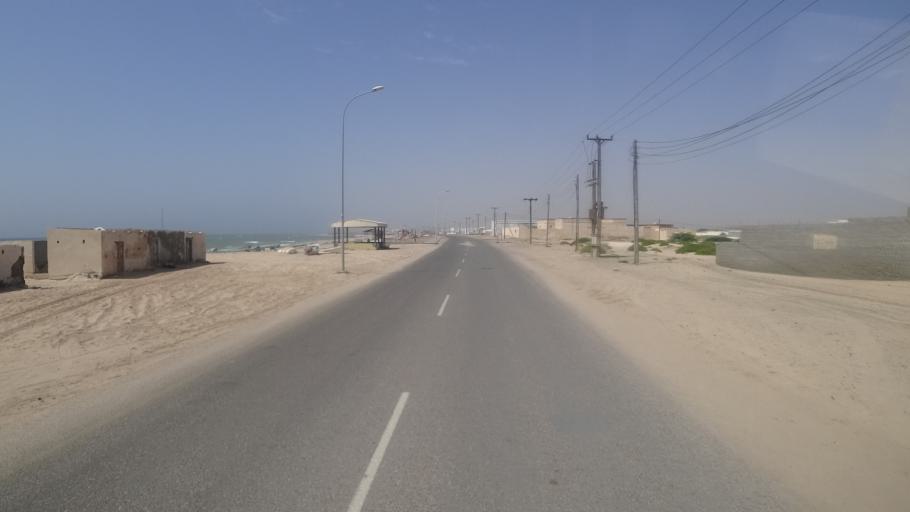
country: OM
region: Ash Sharqiyah
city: Sur
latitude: 22.1165
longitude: 59.7139
